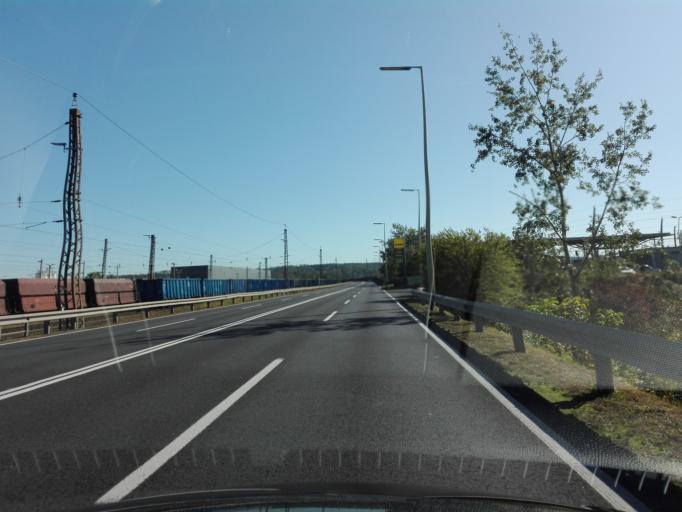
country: AT
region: Upper Austria
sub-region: Politischer Bezirk Urfahr-Umgebung
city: Steyregg
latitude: 48.2642
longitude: 14.3228
